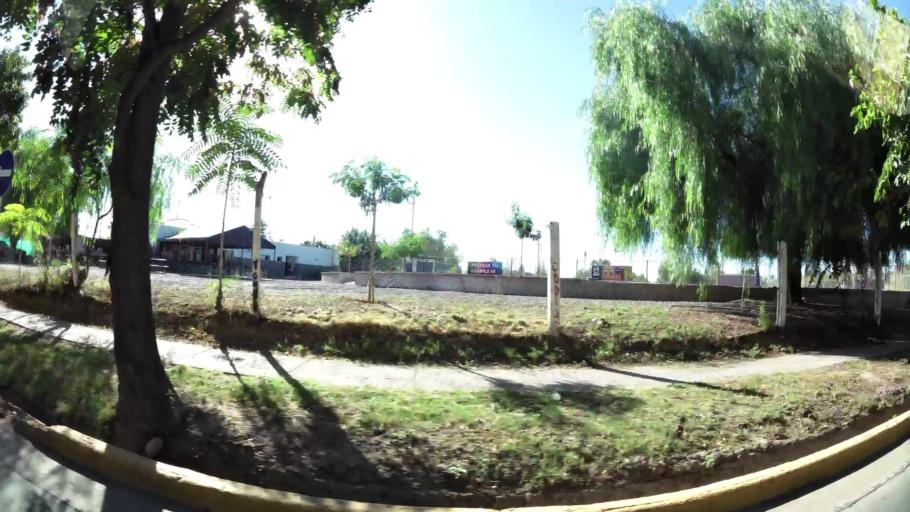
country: AR
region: Mendoza
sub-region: Departamento de Godoy Cruz
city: Godoy Cruz
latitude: -32.9193
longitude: -68.8435
